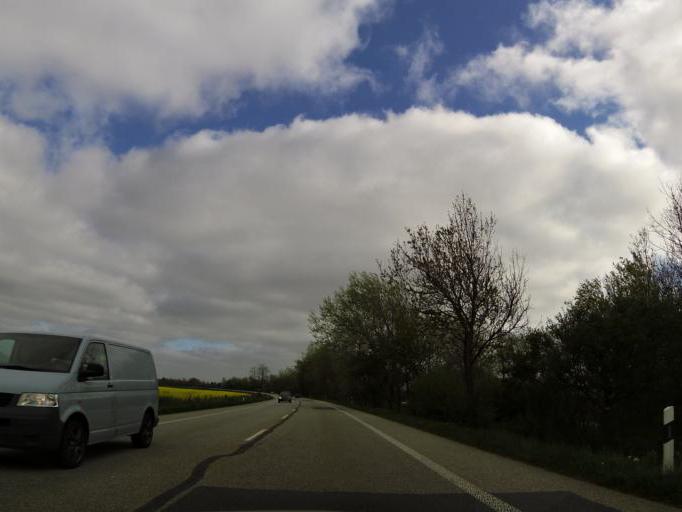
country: DE
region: Schleswig-Holstein
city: Risum-Lindholm
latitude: 54.7768
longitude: 8.8558
